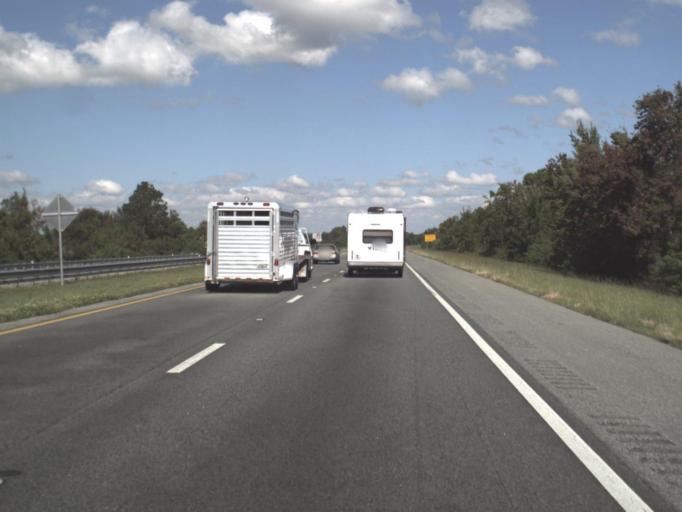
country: US
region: Florida
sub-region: Osceola County
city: Saint Cloud
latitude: 28.1540
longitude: -81.2981
